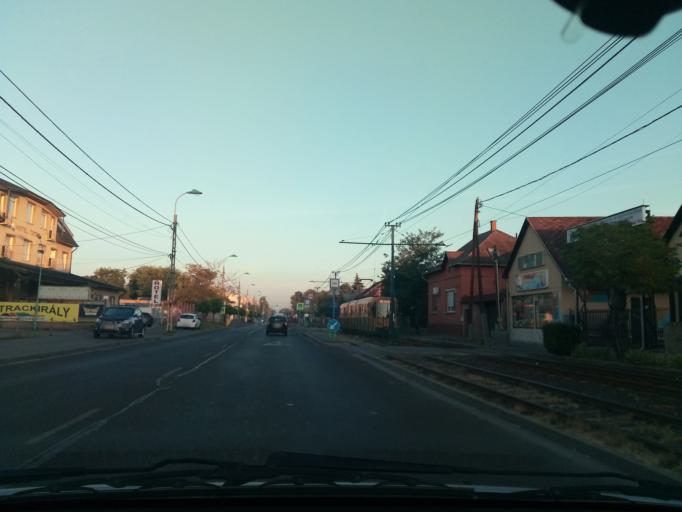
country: HU
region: Budapest
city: Budapest XVIII. keruelet
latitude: 47.4494
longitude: 19.1638
